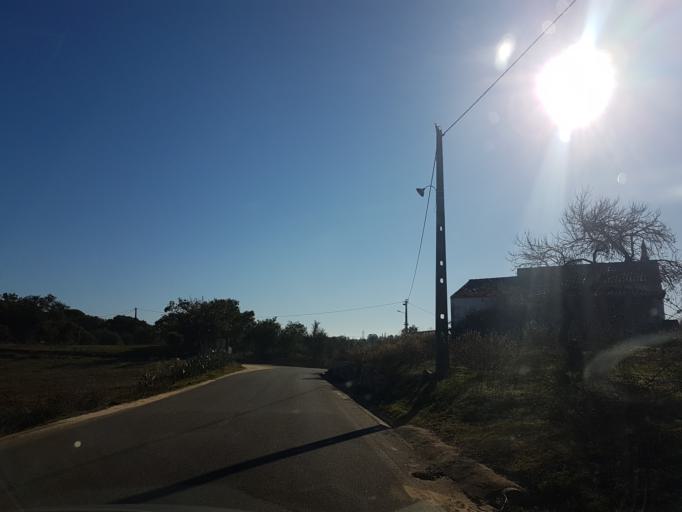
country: PT
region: Faro
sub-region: Lagoa
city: Carvoeiro
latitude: 37.1061
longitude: -8.4311
